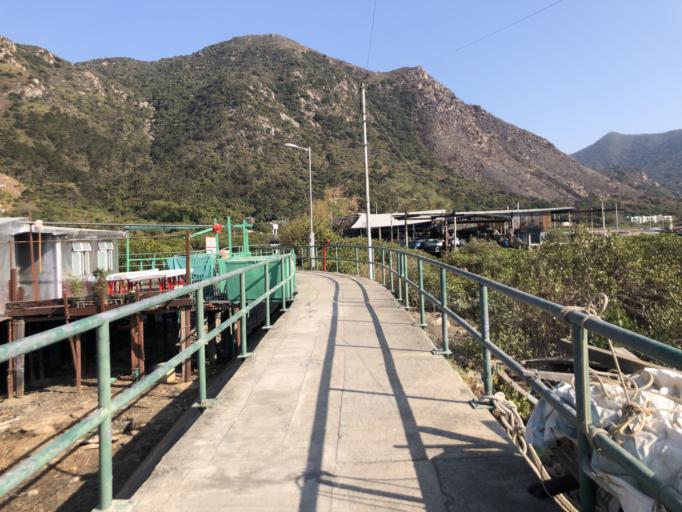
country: HK
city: Tai O
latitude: 22.2551
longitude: 113.8663
